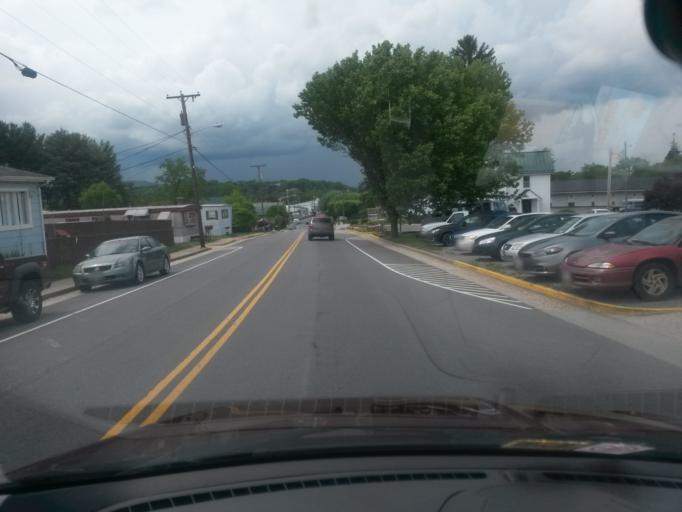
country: US
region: Virginia
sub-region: Floyd County
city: Floyd
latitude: 36.9087
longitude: -80.3181
